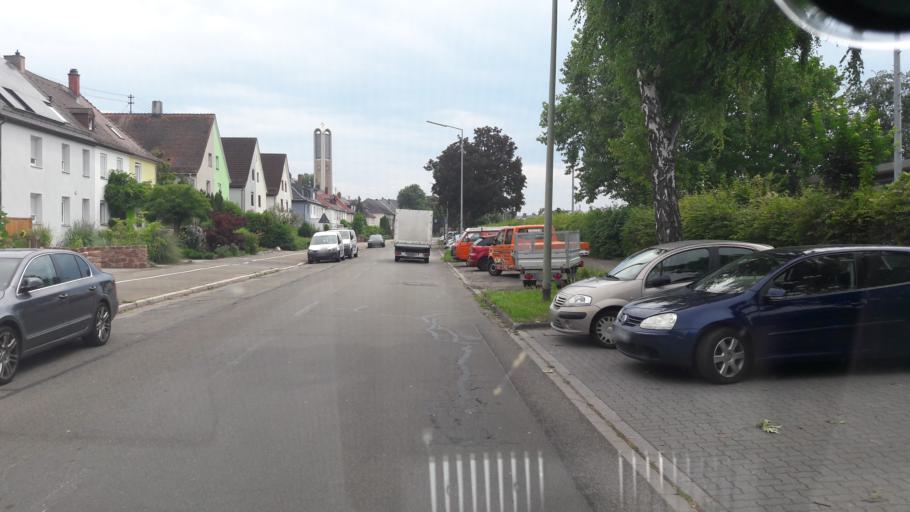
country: DE
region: Baden-Wuerttemberg
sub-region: Karlsruhe Region
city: Karlsruhe
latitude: 49.0258
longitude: 8.3657
